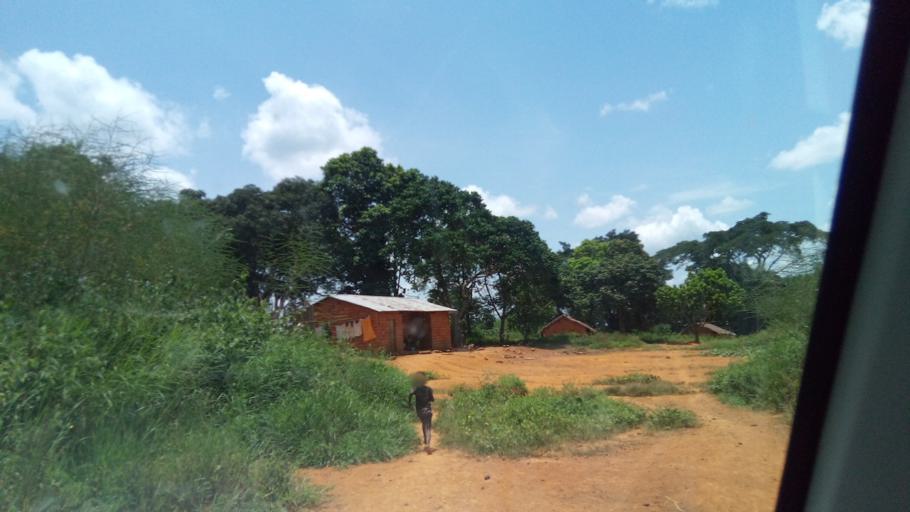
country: AO
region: Zaire
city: Mbanza Congo
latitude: -5.8064
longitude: 14.2380
